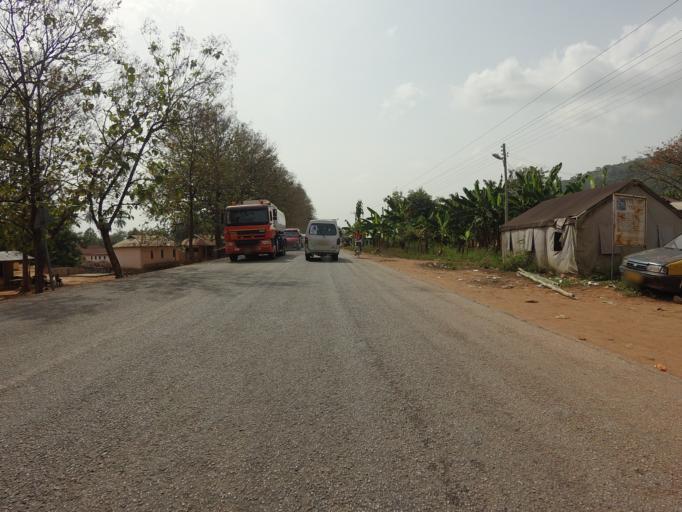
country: GH
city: Akropong
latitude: 6.2836
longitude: 0.1317
